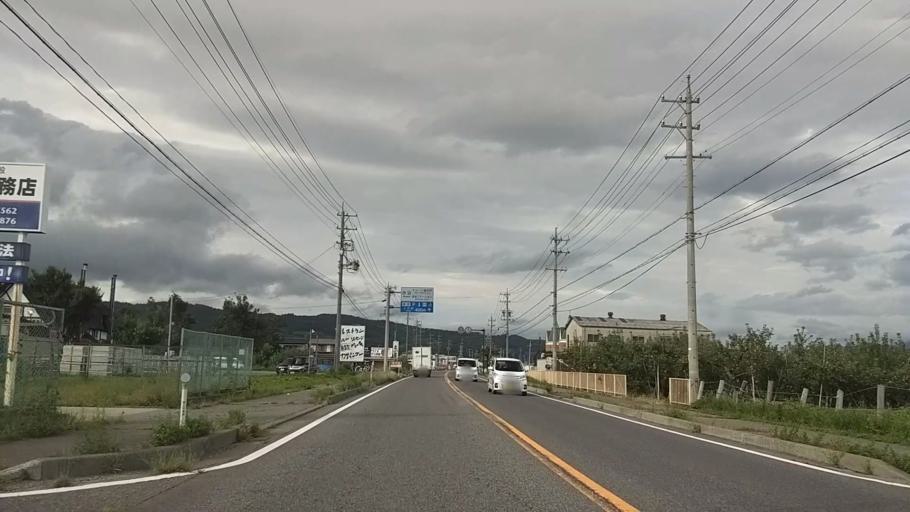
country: JP
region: Nagano
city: Suzaka
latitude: 36.6907
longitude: 138.2683
